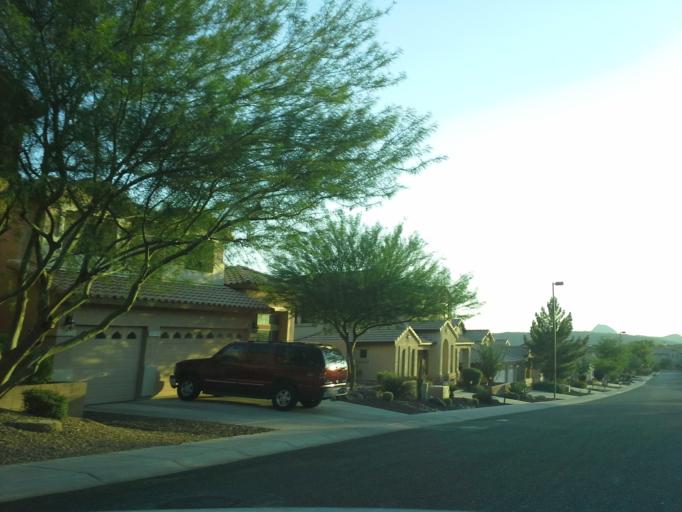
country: US
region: Arizona
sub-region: Maricopa County
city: Anthem
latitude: 33.7535
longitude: -112.1014
